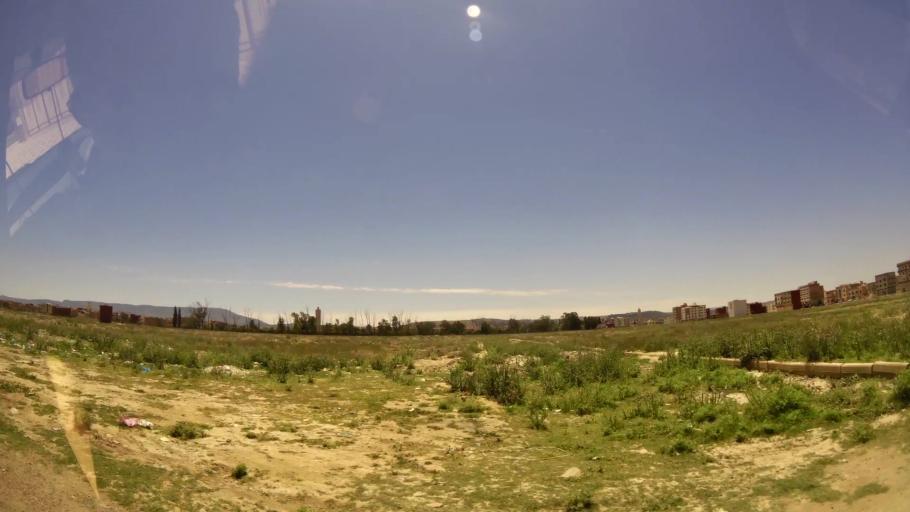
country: MA
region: Oriental
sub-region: Oujda-Angad
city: Oujda
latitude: 34.6740
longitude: -1.8731
